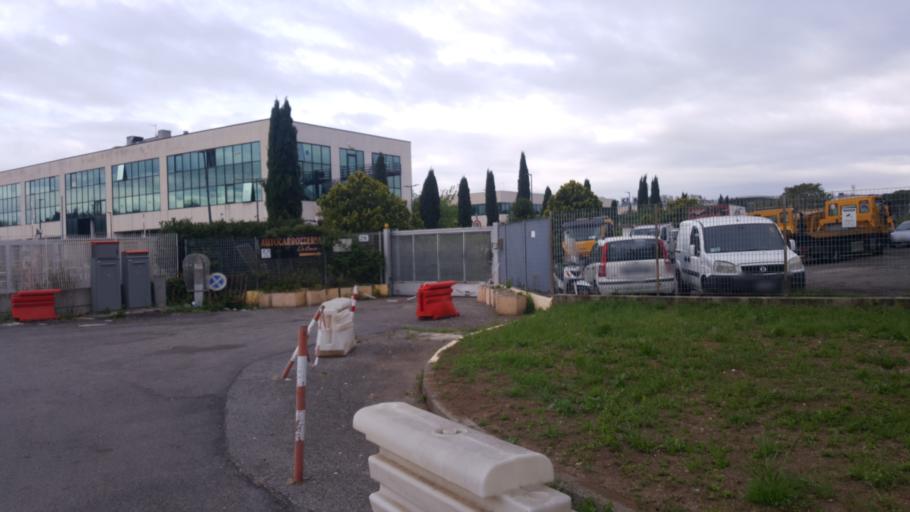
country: IT
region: Latium
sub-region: Citta metropolitana di Roma Capitale
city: Setteville
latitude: 41.9302
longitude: 12.6094
